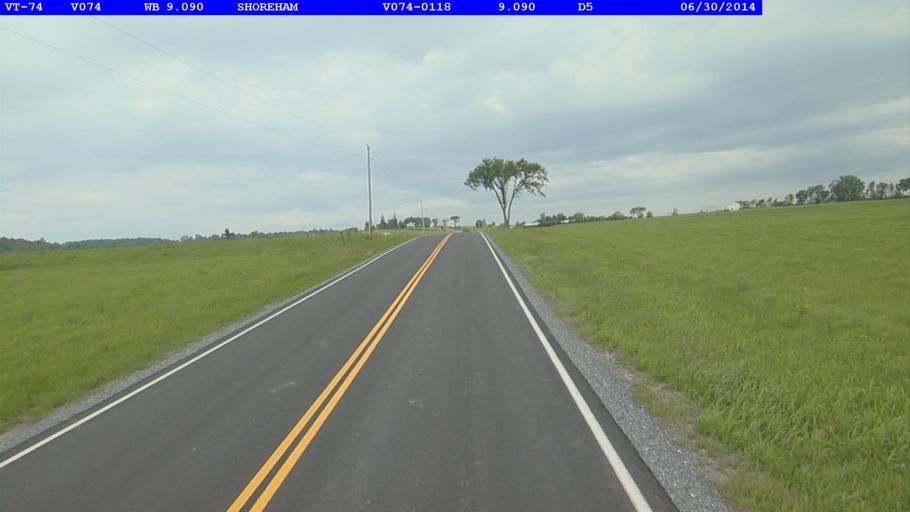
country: US
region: Vermont
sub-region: Addison County
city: Middlebury (village)
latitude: 43.9423
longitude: -73.2728
